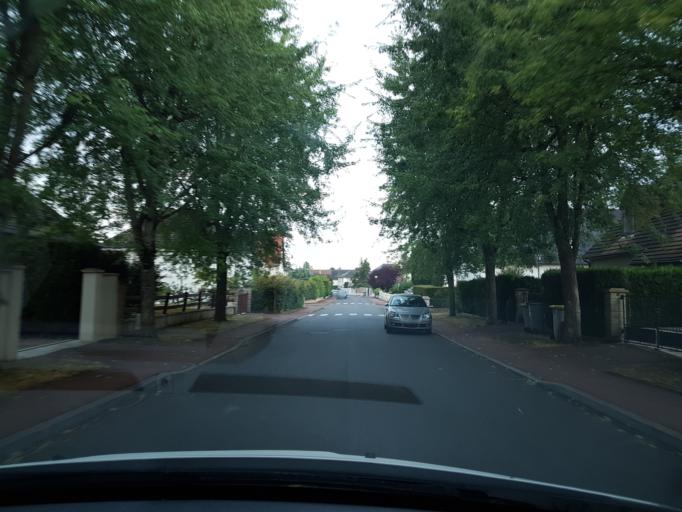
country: FR
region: Centre
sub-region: Departement d'Indre-et-Loire
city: Chambray-les-Tours
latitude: 47.3368
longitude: 0.7125
